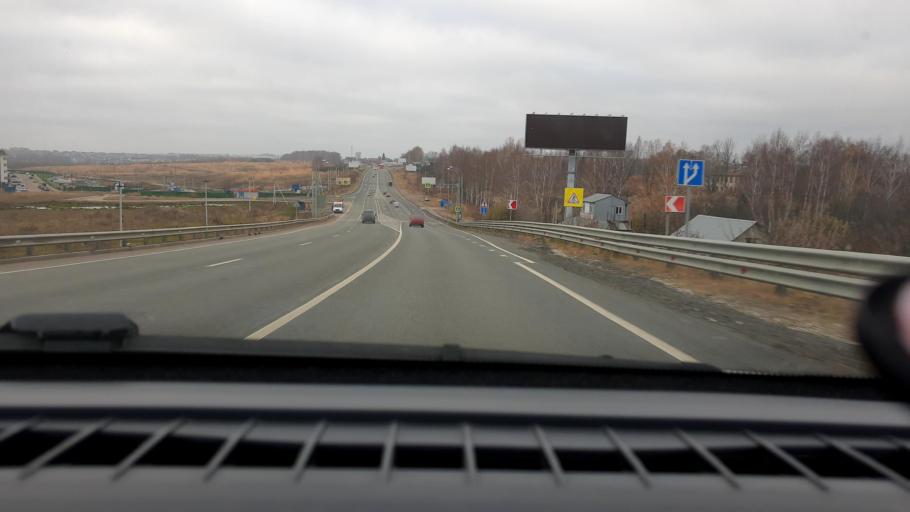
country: RU
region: Nizjnij Novgorod
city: Burevestnik
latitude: 56.2153
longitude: 43.9074
